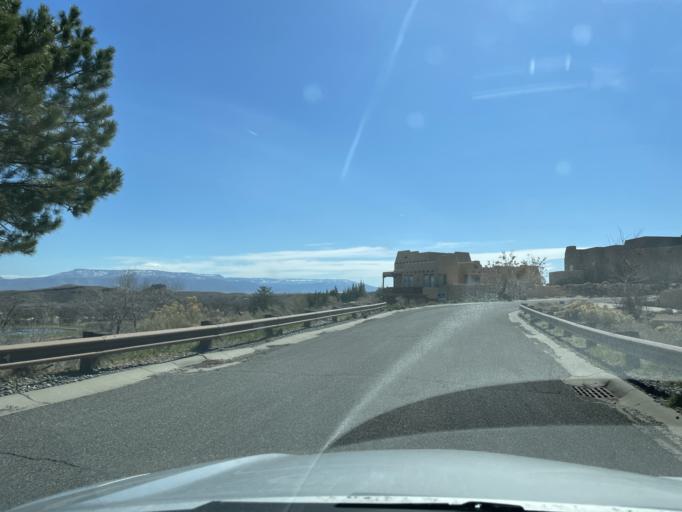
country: US
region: Colorado
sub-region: Mesa County
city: Redlands
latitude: 39.0753
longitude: -108.6710
